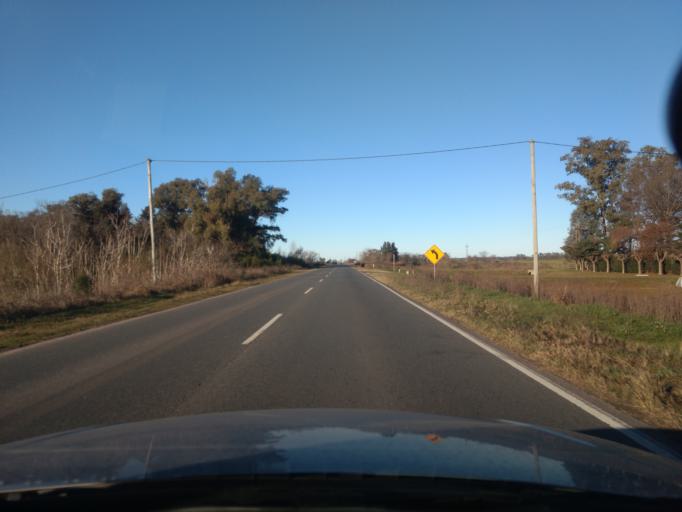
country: AR
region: Buenos Aires
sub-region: Partido de Lujan
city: Lujan
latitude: -34.6252
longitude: -59.1082
